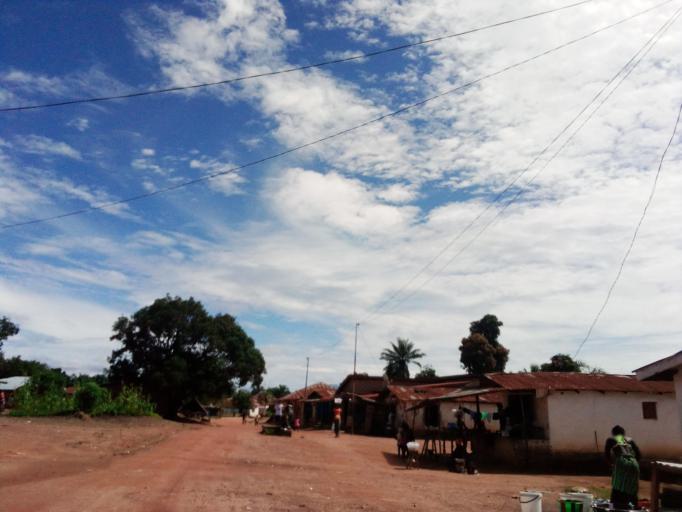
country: SL
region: Eastern Province
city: Koidu
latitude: 8.6508
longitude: -10.9615
